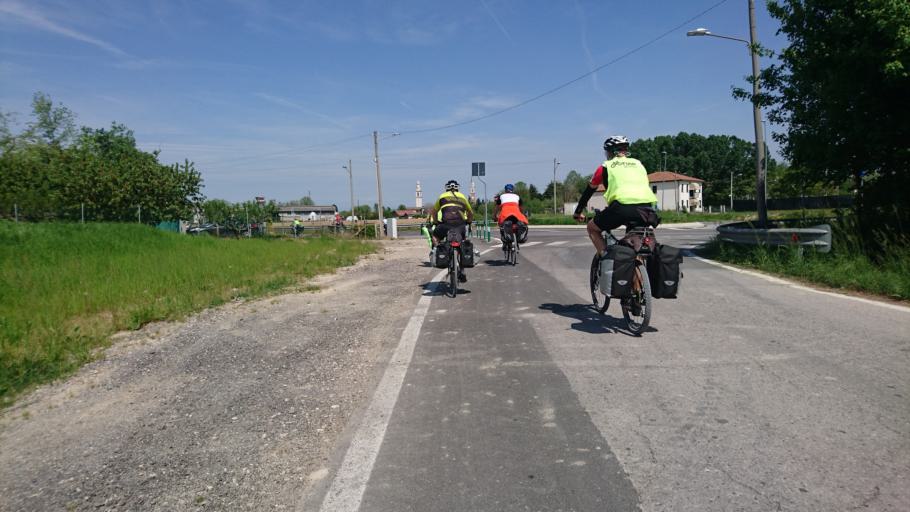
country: IT
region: Veneto
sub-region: Provincia di Padova
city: Vigodarzere
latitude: 45.4466
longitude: 11.8836
